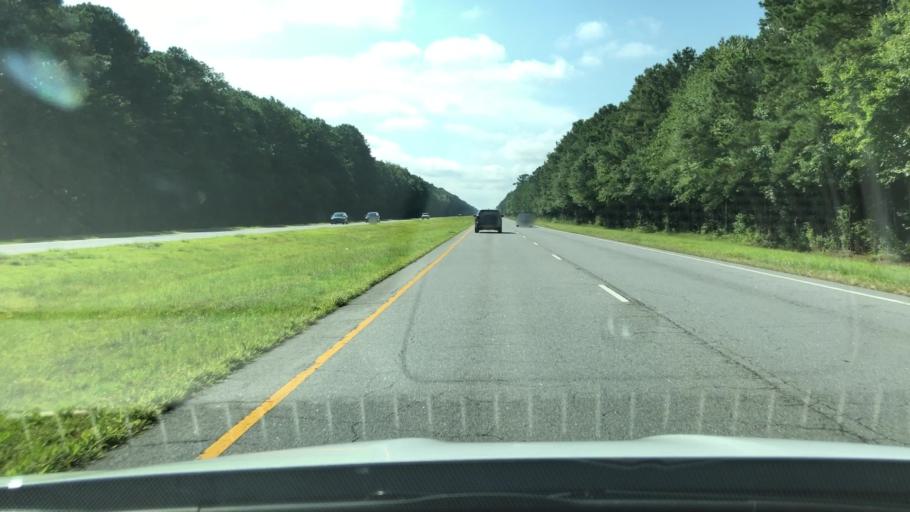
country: US
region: North Carolina
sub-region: Pasquotank County
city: Elizabeth City
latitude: 36.4031
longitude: -76.3349
